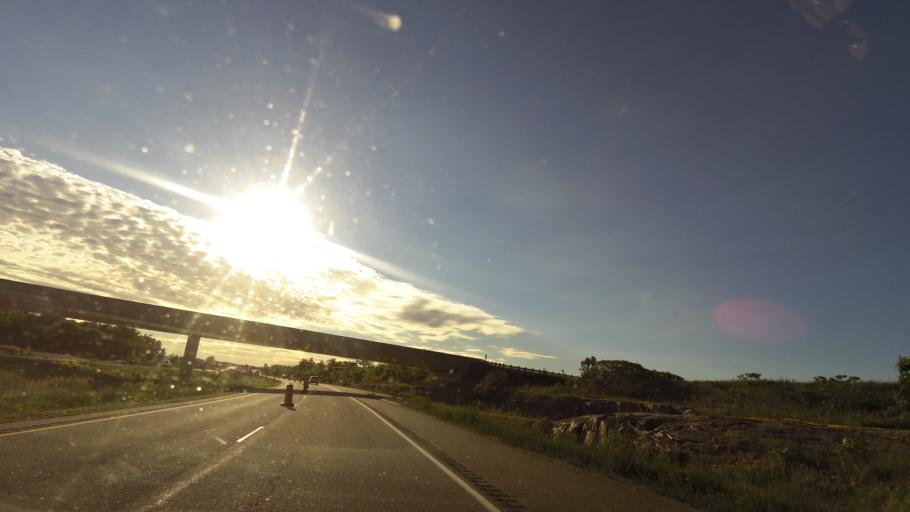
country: CA
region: Ontario
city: Midland
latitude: 44.7978
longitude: -79.7128
